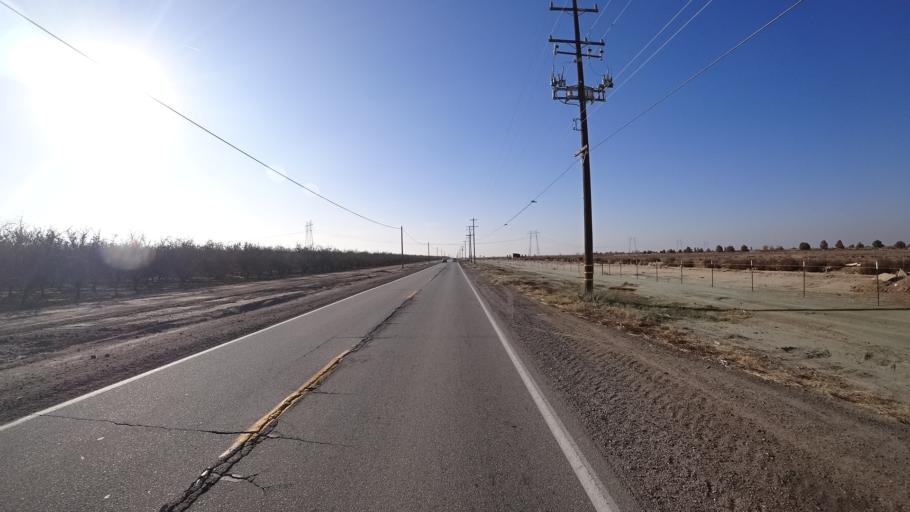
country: US
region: California
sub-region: Kern County
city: Rosedale
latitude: 35.2962
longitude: -119.1666
